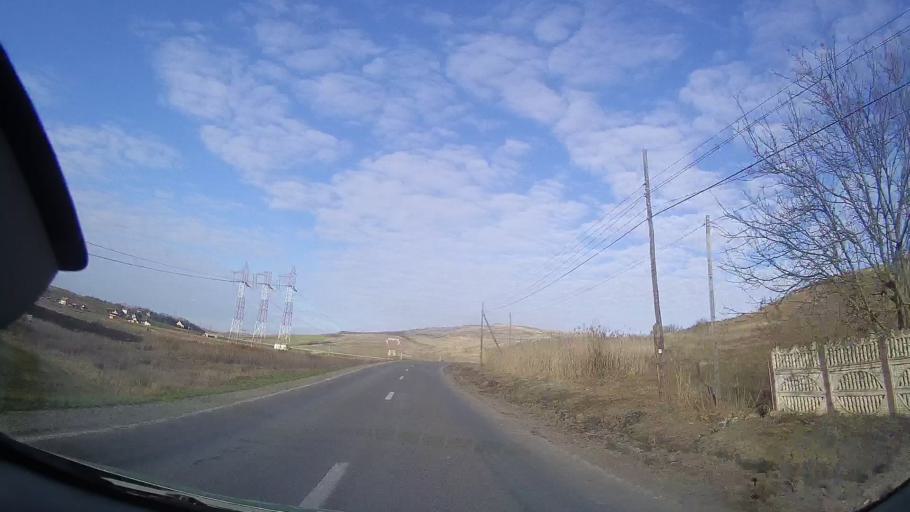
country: RO
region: Cluj
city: Caianu Mic
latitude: 46.8088
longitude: 23.8727
